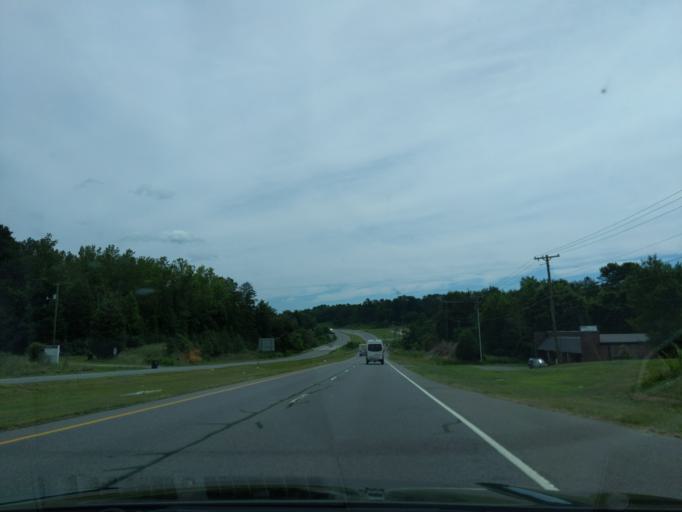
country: US
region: North Carolina
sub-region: Cabarrus County
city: Concord
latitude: 35.3753
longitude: -80.5403
